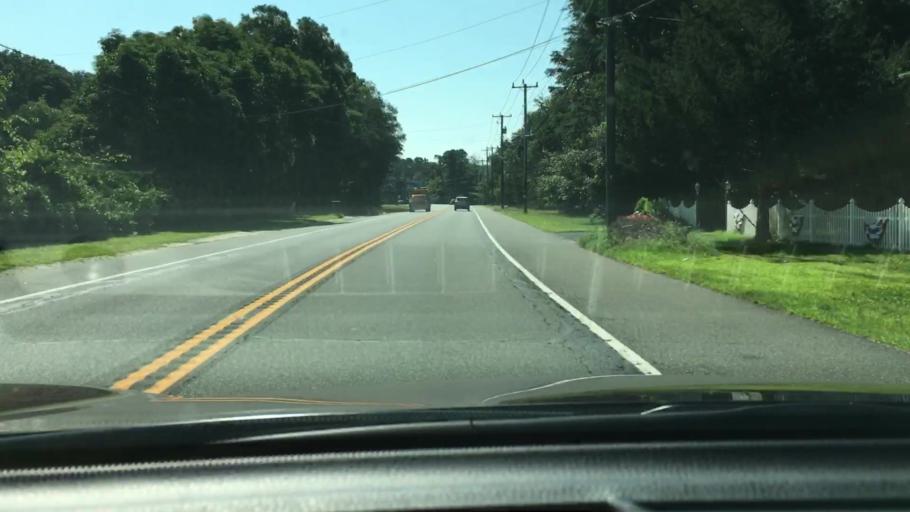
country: US
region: New Jersey
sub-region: Cumberland County
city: Laurel Lake
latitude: 39.3721
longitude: -74.9435
